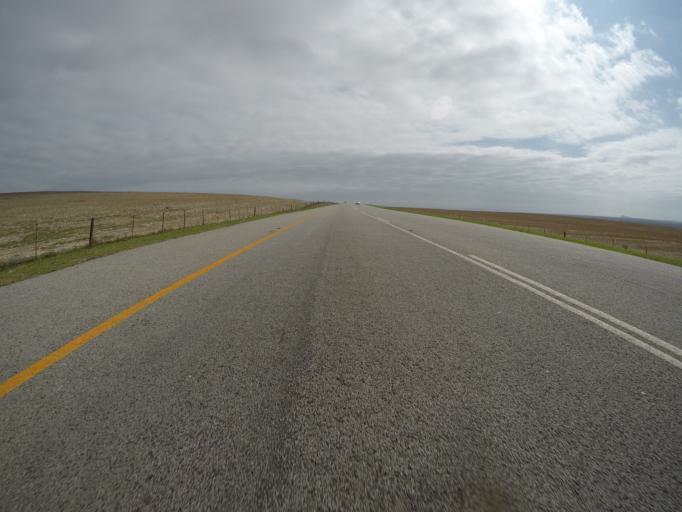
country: ZA
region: Western Cape
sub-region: City of Cape Town
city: Sunset Beach
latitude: -33.7239
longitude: 18.4996
